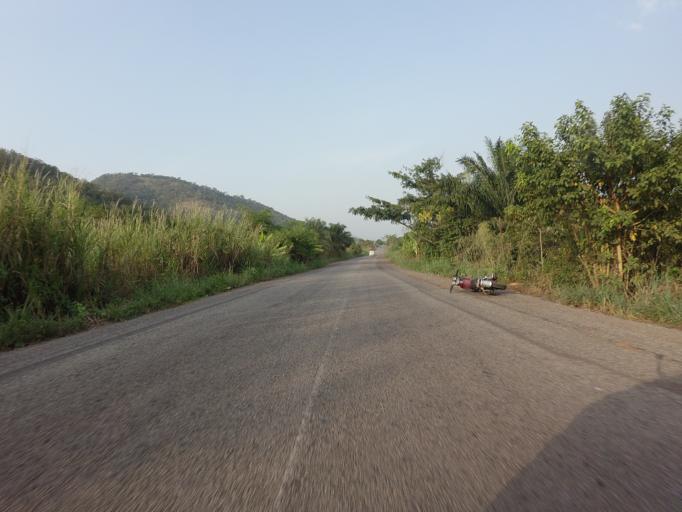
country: GH
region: Volta
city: Ho
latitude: 6.5576
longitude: 0.2958
